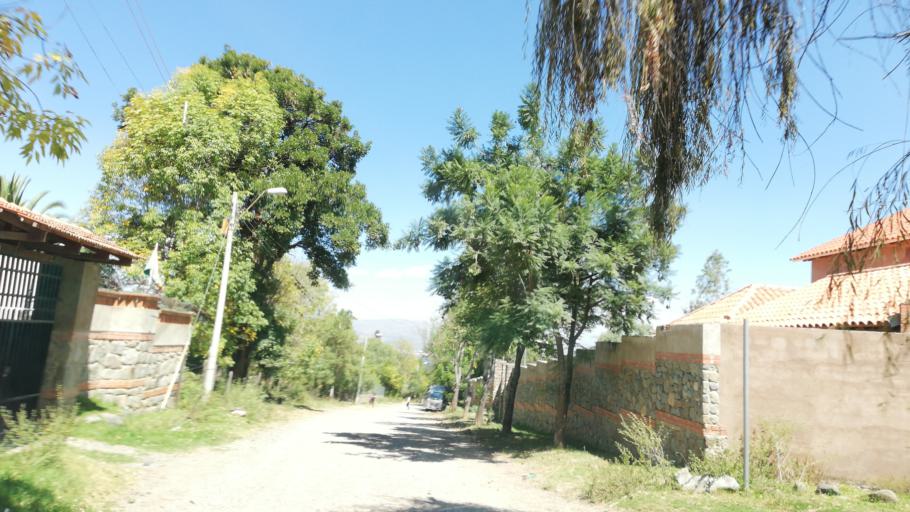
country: BO
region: Cochabamba
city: Cochabamba
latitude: -17.3217
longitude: -66.2123
